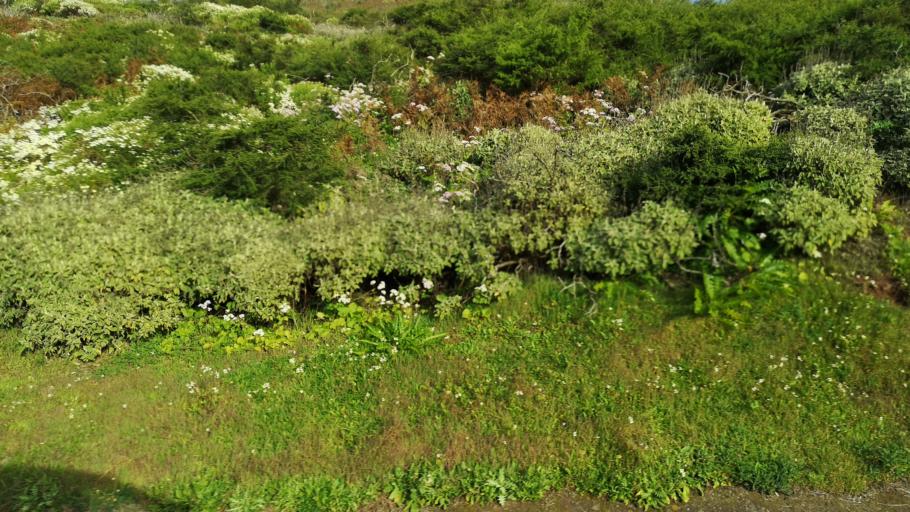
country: ES
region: Canary Islands
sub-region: Provincia de Santa Cruz de Tenerife
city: Alajero
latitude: 28.0953
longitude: -17.2469
